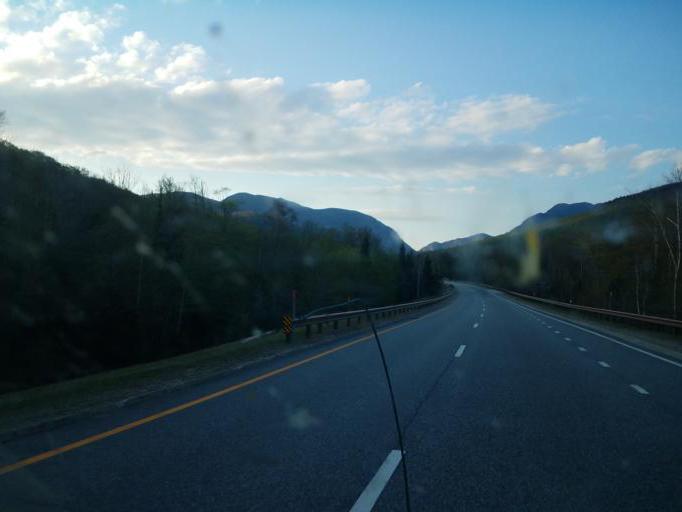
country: US
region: New Hampshire
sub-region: Grafton County
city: Woodstock
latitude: 44.1091
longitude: -71.6826
